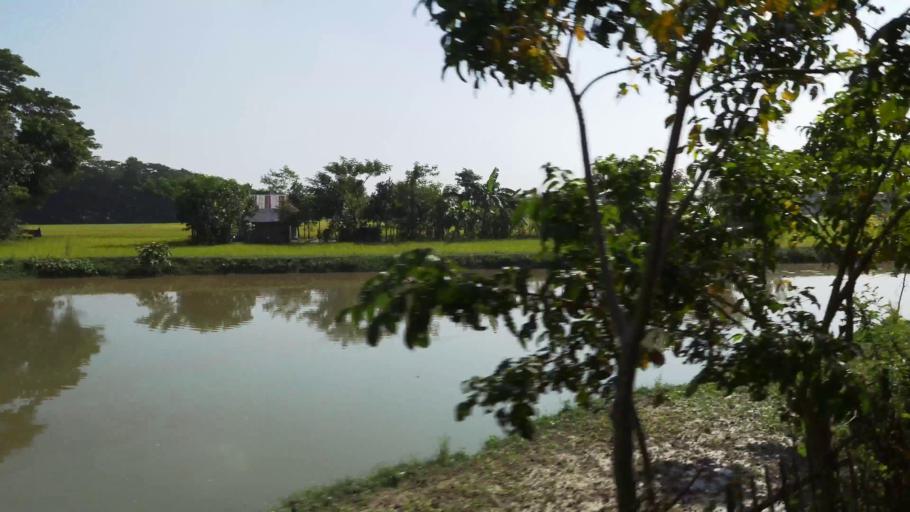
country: BD
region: Dhaka
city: Gafargaon
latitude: 24.5109
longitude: 90.5144
